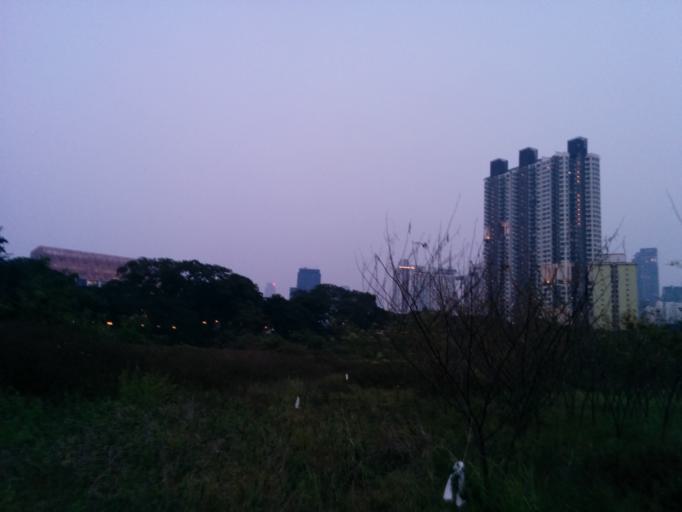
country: SG
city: Singapore
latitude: 1.2753
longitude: 103.8329
